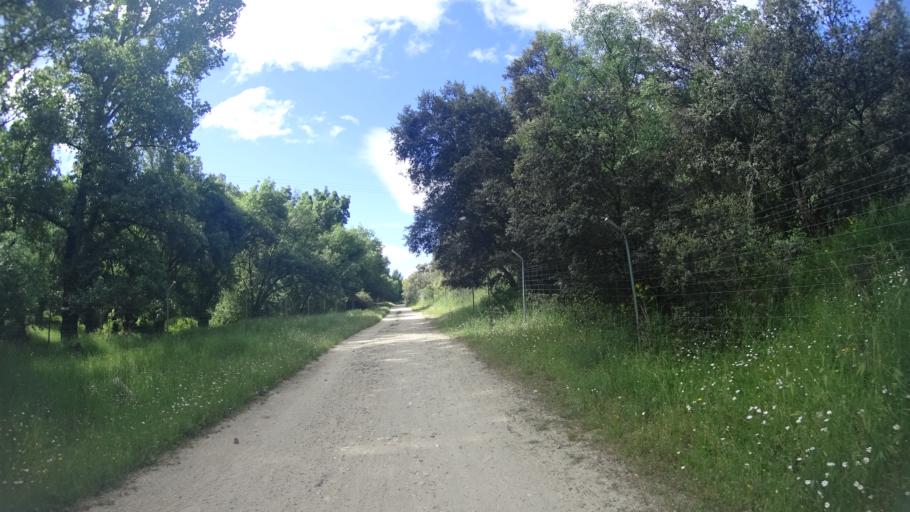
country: ES
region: Madrid
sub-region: Provincia de Madrid
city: Villanueva del Pardillo
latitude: 40.4330
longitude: -3.9530
